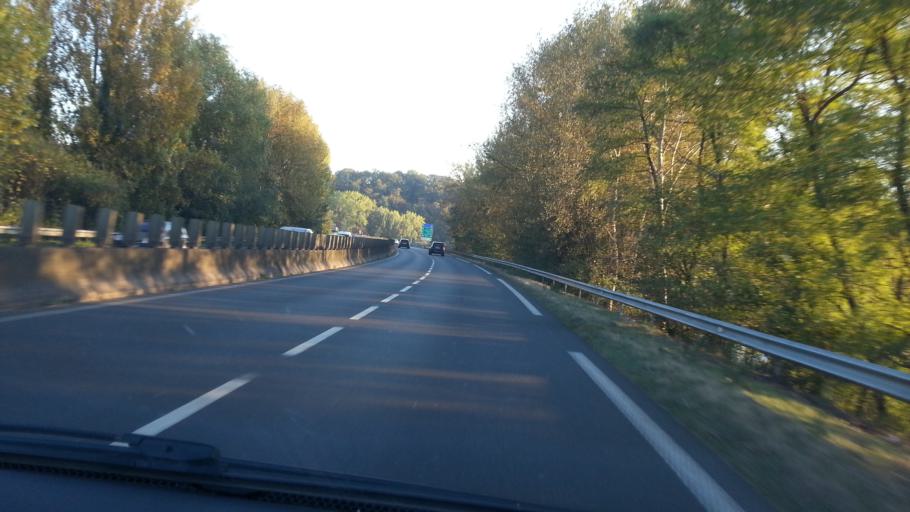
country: FR
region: Picardie
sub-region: Departement de l'Oise
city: Creil
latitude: 49.2672
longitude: 2.4846
